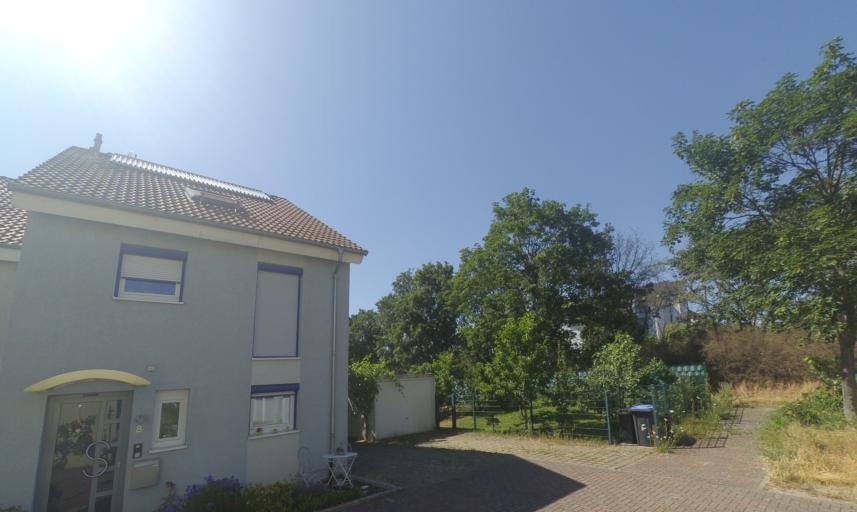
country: DE
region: Rheinland-Pfalz
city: Limburgerhof
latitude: 49.4242
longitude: 8.3963
